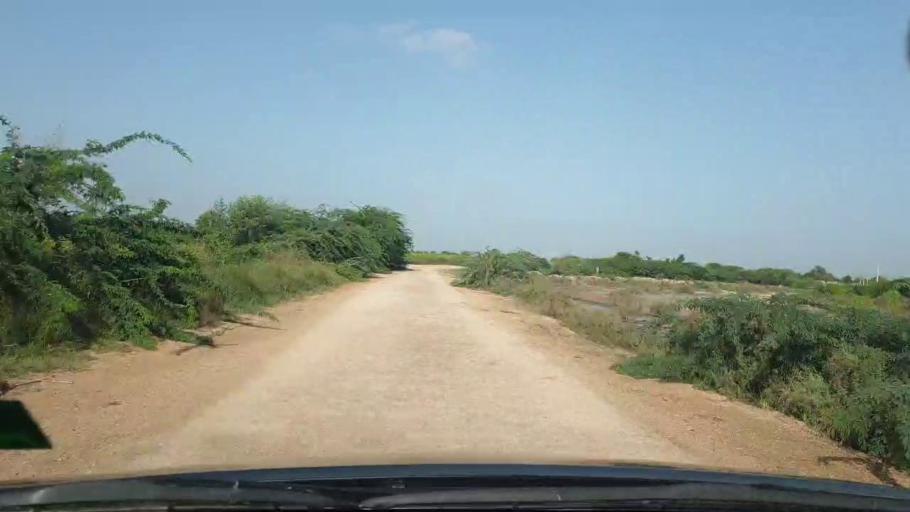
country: PK
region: Sindh
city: Tando Bago
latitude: 24.6850
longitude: 69.0121
